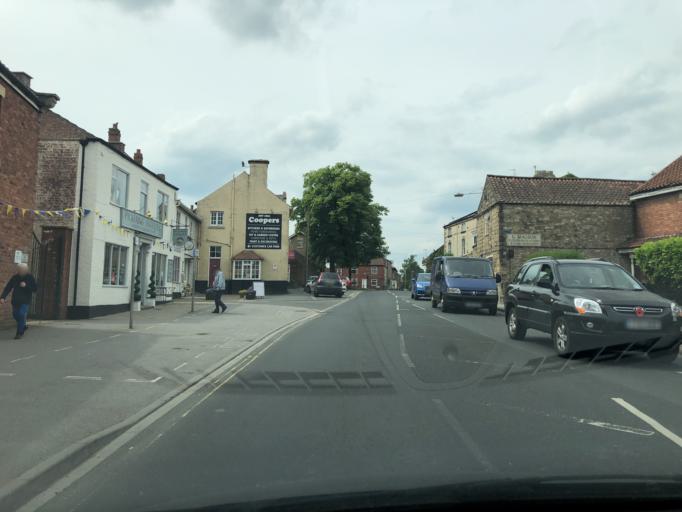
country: GB
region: England
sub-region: North Yorkshire
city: Pickering
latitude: 54.2449
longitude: -0.7805
